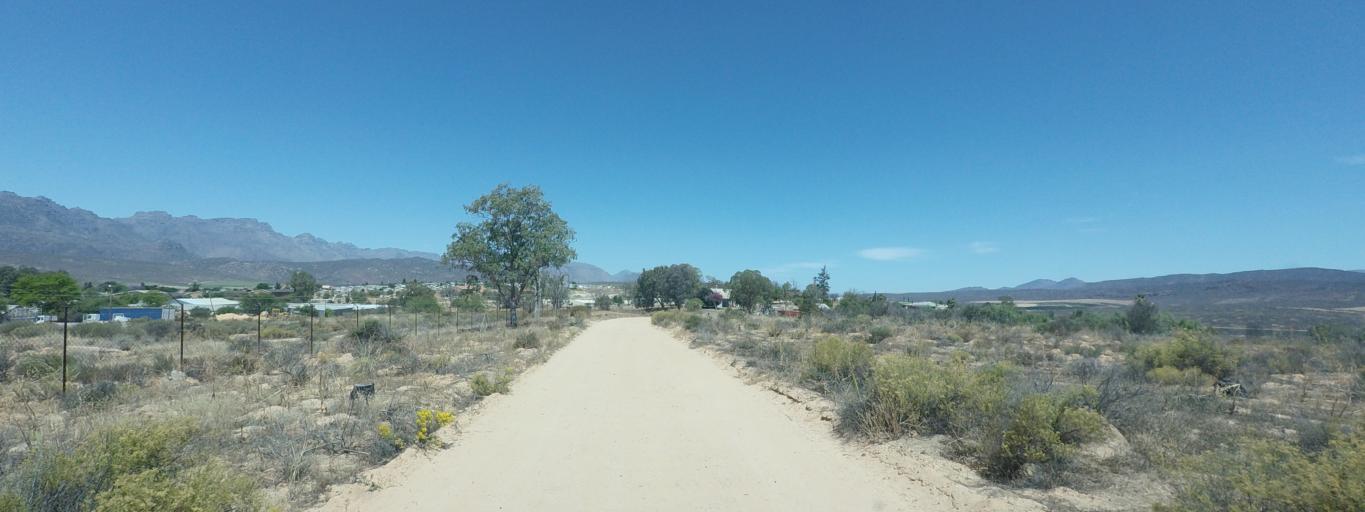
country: ZA
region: Western Cape
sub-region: West Coast District Municipality
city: Clanwilliam
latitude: -32.1883
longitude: 18.8851
